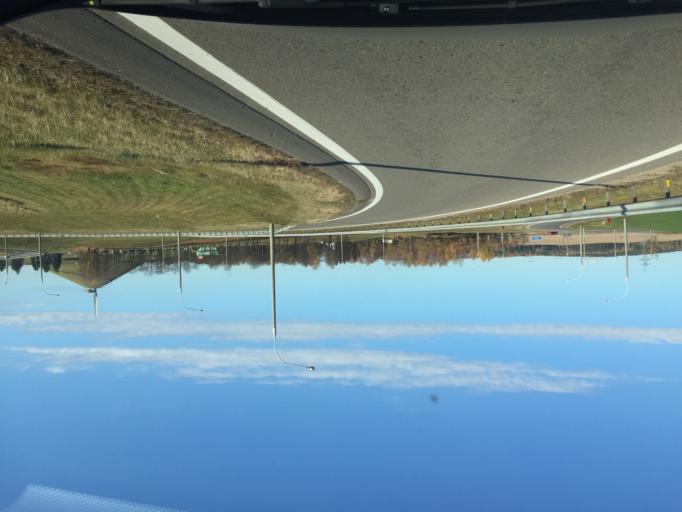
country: BY
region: Minsk
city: Slabada
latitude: 54.0170
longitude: 27.8866
